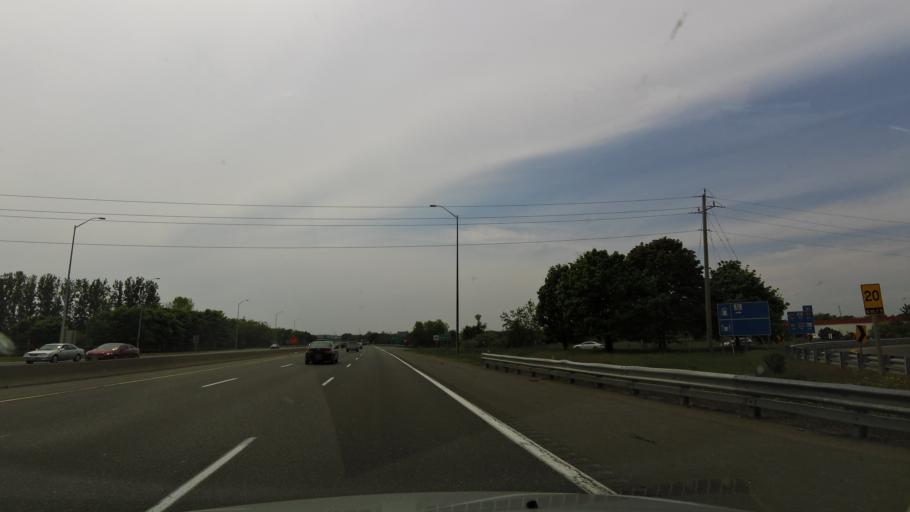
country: CA
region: Ontario
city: Oshawa
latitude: 43.8989
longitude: -78.6757
